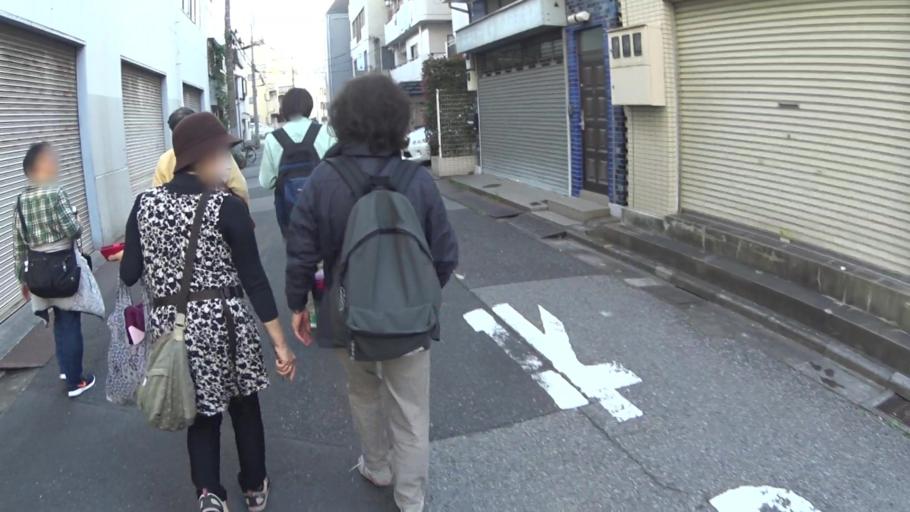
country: JP
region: Tokyo
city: Urayasu
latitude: 35.7107
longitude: 139.8163
